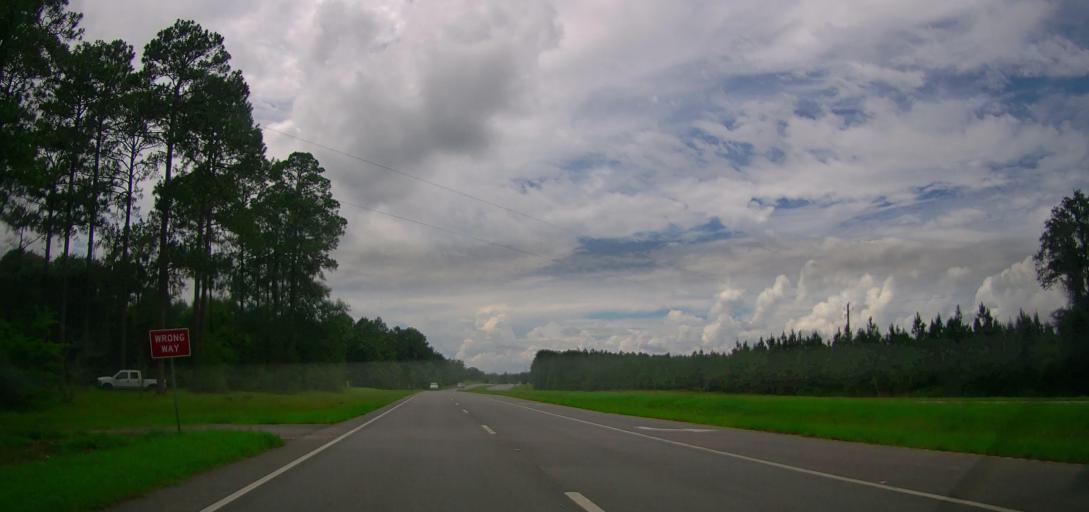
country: US
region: Georgia
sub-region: Telfair County
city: McRae
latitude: 32.0419
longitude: -82.8517
